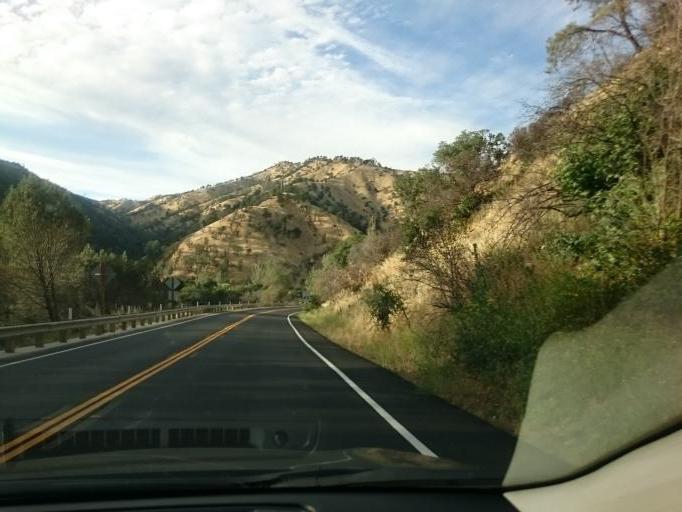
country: US
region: California
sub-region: Yolo County
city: Winters
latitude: 38.5101
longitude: -122.0965
